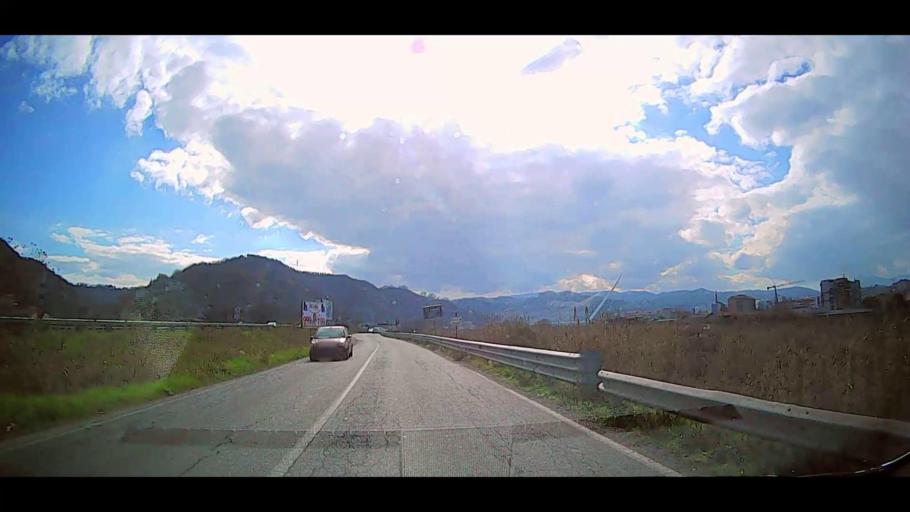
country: IT
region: Calabria
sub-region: Provincia di Cosenza
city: Cosenza
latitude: 39.3067
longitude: 16.2627
